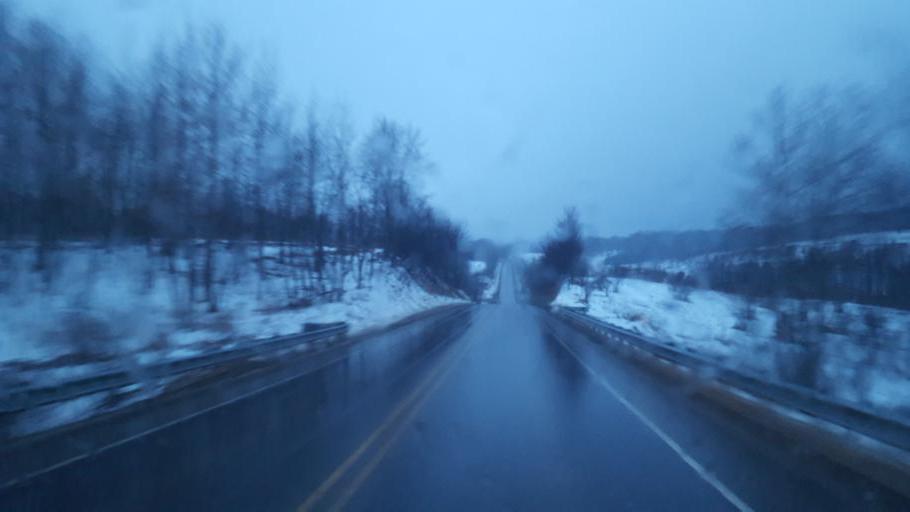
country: US
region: Pennsylvania
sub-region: McKean County
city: Port Allegany
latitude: 41.8250
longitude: -78.3532
